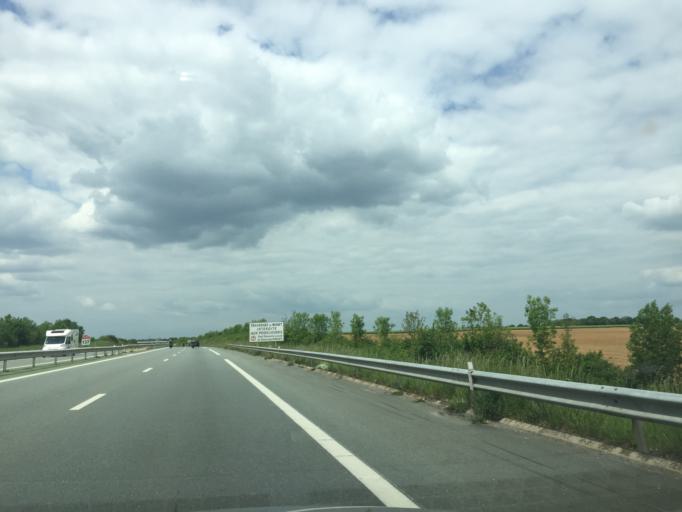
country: FR
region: Poitou-Charentes
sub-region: Departement des Deux-Sevres
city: Saint-Gelais
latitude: 46.3988
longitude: -0.3799
